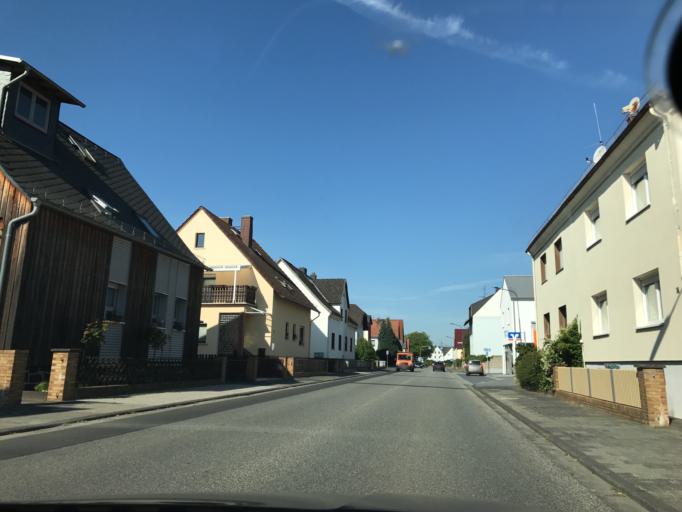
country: DE
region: Hesse
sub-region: Regierungsbezirk Giessen
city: Wetzlar
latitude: 50.5853
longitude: 8.5496
